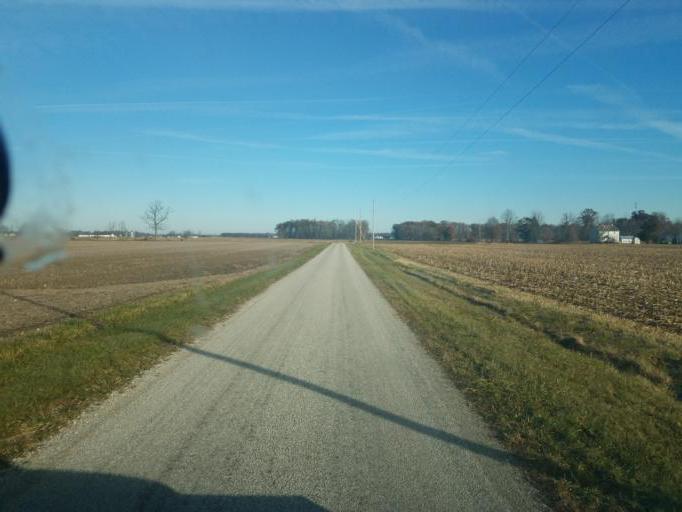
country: US
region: Ohio
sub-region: Crawford County
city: Galion
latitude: 40.7027
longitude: -82.8948
